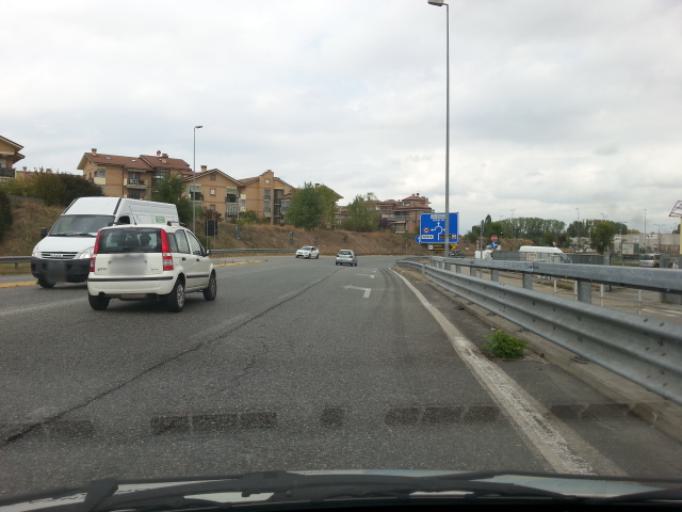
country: IT
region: Piedmont
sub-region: Provincia di Torino
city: Pasta
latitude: 45.0112
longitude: 7.5556
